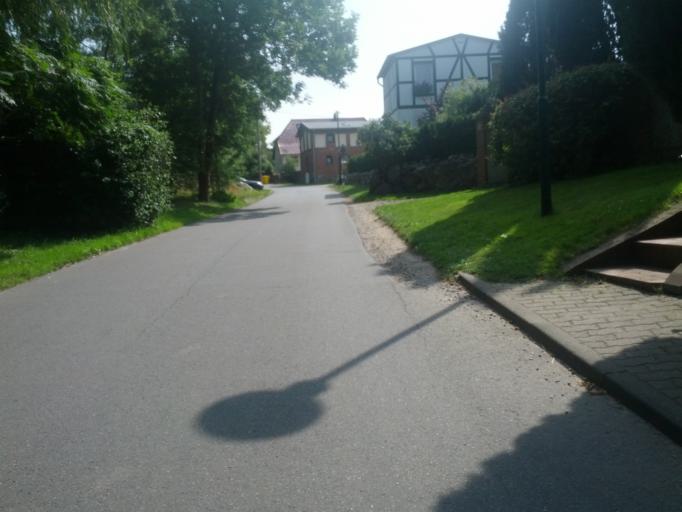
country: DE
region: Mecklenburg-Vorpommern
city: Bastorf
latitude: 54.1359
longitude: 11.6807
